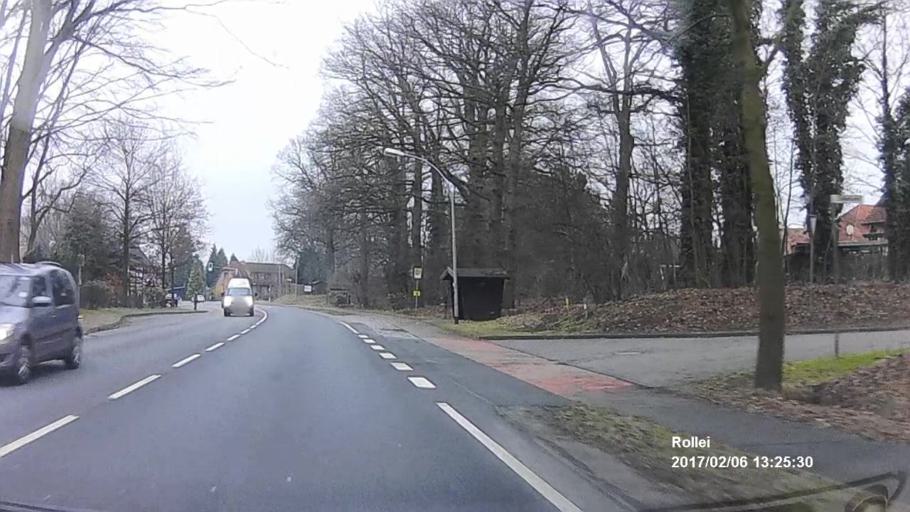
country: DE
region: Lower Saxony
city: Bomlitz
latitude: 52.8666
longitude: 9.6317
